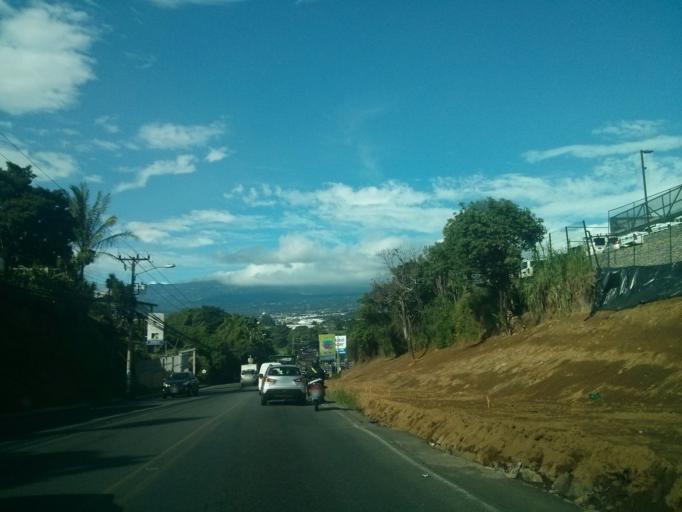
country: CR
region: San Jose
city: Colima
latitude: 9.9555
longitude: -84.1110
